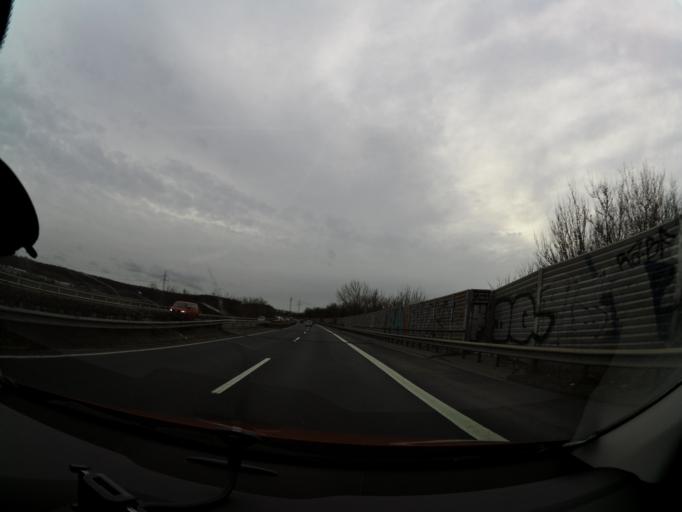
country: DE
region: Lower Saxony
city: Leiferde
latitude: 52.1599
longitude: 10.4917
